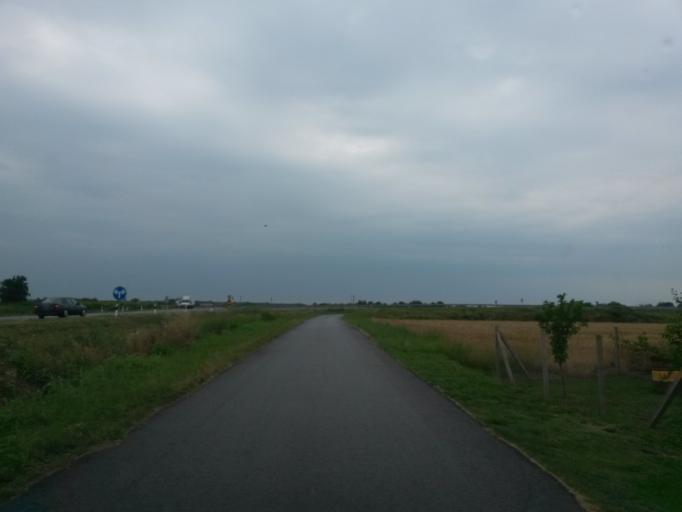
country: HR
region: Vukovarsko-Srijemska
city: Ilok
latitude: 45.2188
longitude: 19.3531
